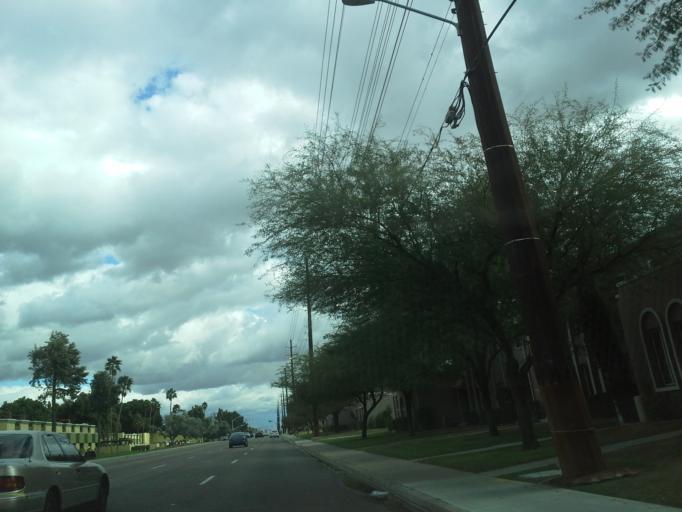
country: US
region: Arizona
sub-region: Maricopa County
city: Paradise Valley
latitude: 33.4800
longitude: -111.9563
